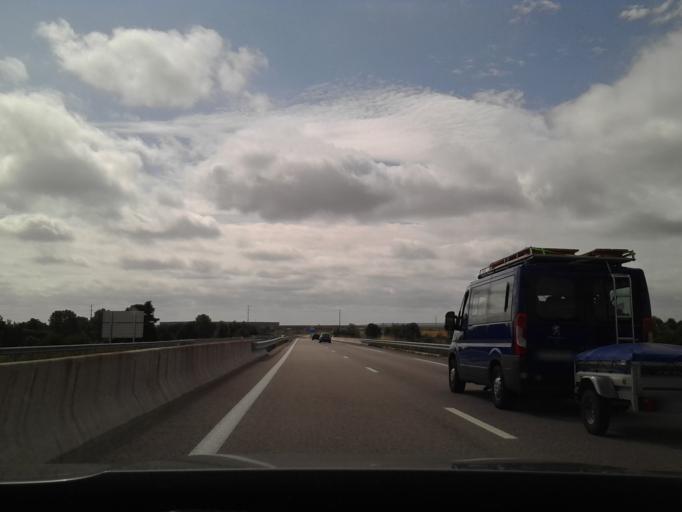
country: FR
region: Lower Normandy
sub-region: Departement de l'Orne
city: Argentan
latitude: 48.7311
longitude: -0.0668
